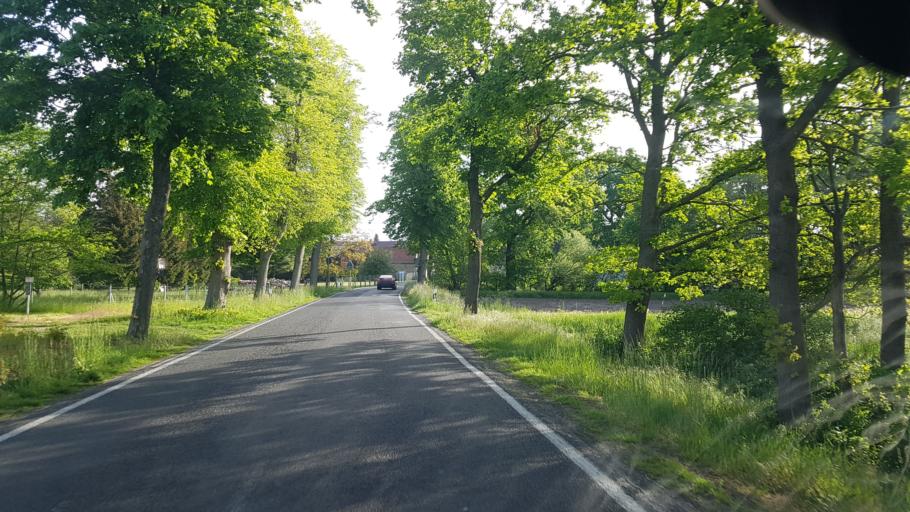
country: DE
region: Brandenburg
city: Dahme
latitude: 51.8841
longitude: 13.4549
